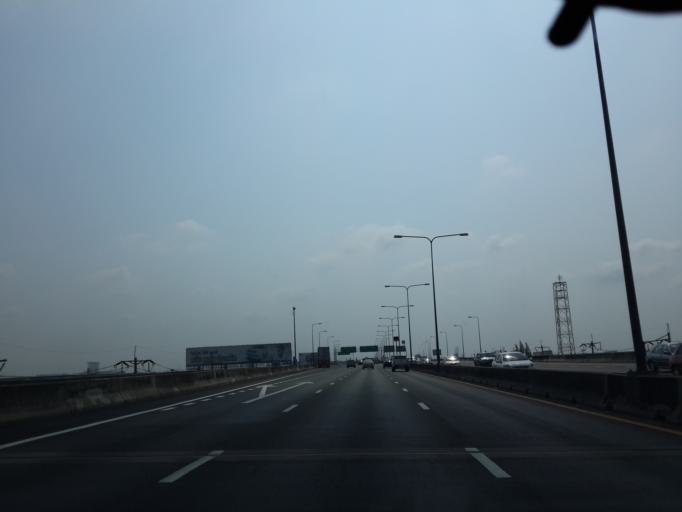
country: TH
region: Bangkok
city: Bang Na
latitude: 13.6255
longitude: 100.7273
